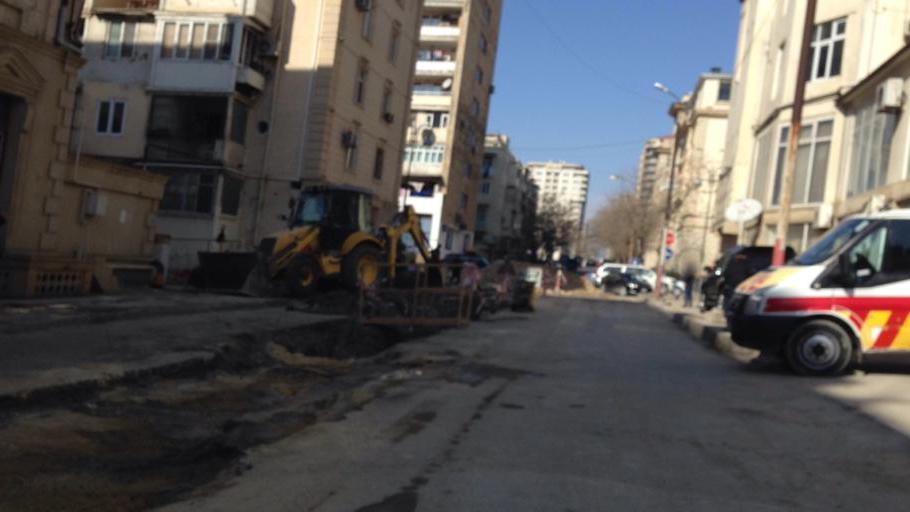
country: AZ
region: Baki
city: Baku
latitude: 40.3901
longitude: 49.8443
